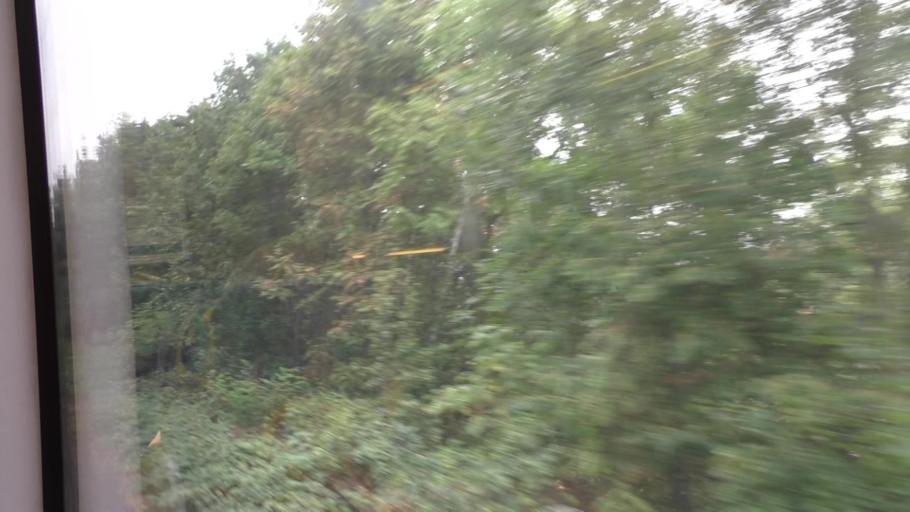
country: DE
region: Saxony
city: Zittau
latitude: 50.9071
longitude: 14.8183
